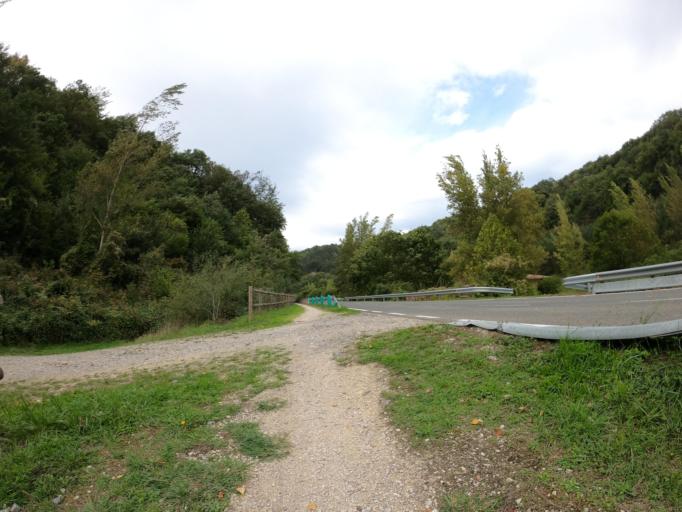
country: ES
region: Navarre
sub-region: Provincia de Navarra
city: Lekunberri
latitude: 42.9733
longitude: -1.8462
